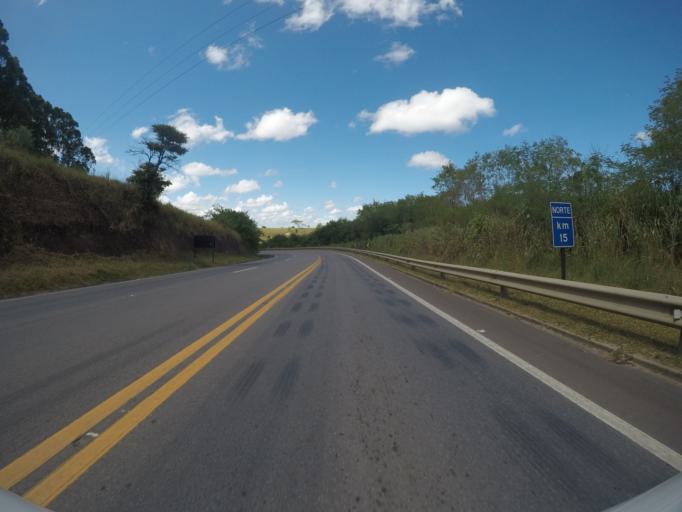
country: BR
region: Espirito Santo
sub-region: Conceicao Da Barra
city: Conceicao da Barra
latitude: -18.2884
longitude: -39.9541
